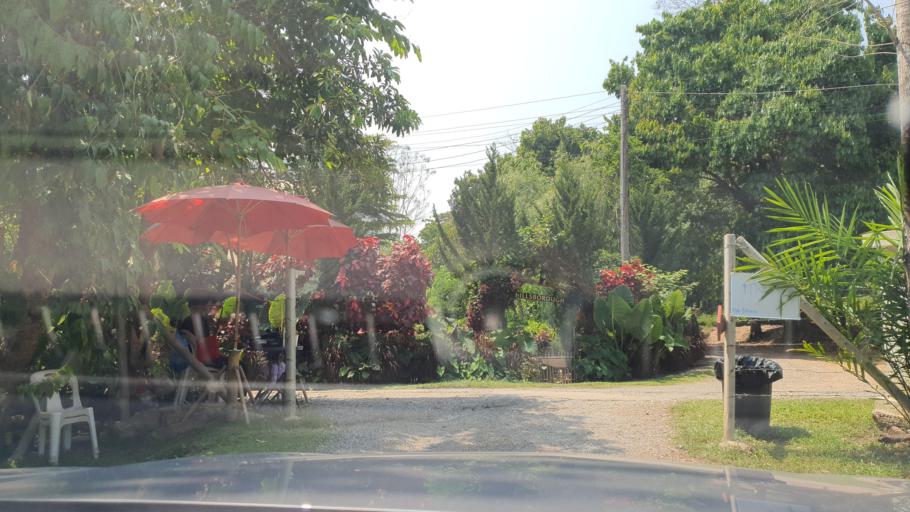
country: TH
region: Chiang Mai
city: Samoeng
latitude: 18.7898
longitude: 98.8407
